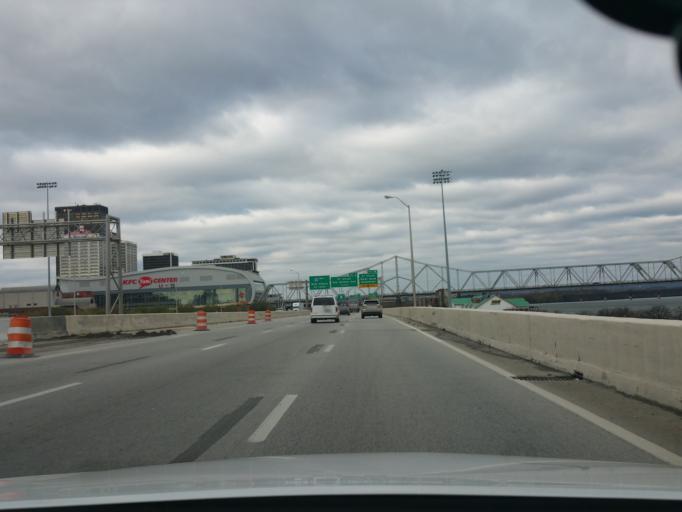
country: US
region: Kentucky
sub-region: Jefferson County
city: Louisville
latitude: 38.2587
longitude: -85.7467
